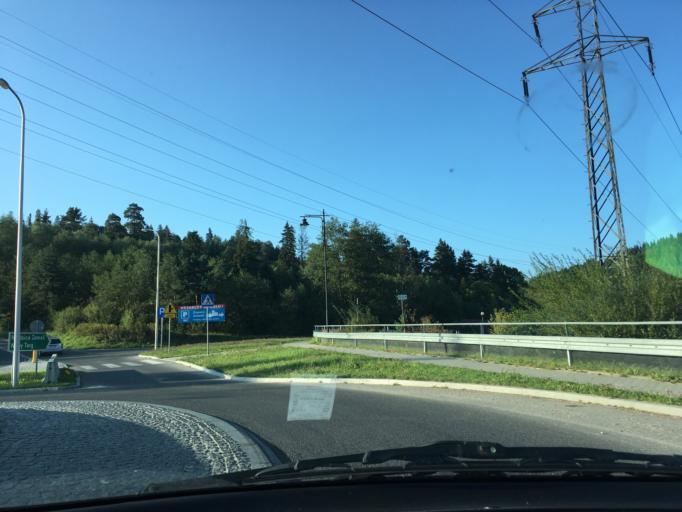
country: PL
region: Lesser Poland Voivodeship
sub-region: Powiat nowotarski
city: Niedzica
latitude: 49.4155
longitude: 20.3201
